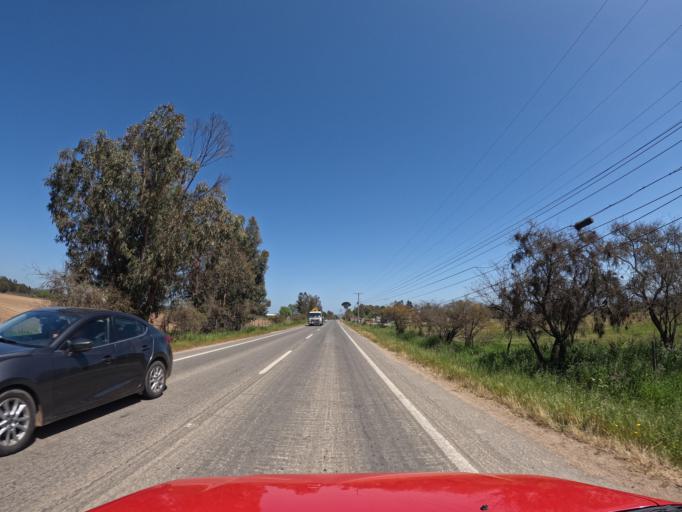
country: CL
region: O'Higgins
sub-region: Provincia de Colchagua
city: Santa Cruz
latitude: -34.7334
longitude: -71.6871
